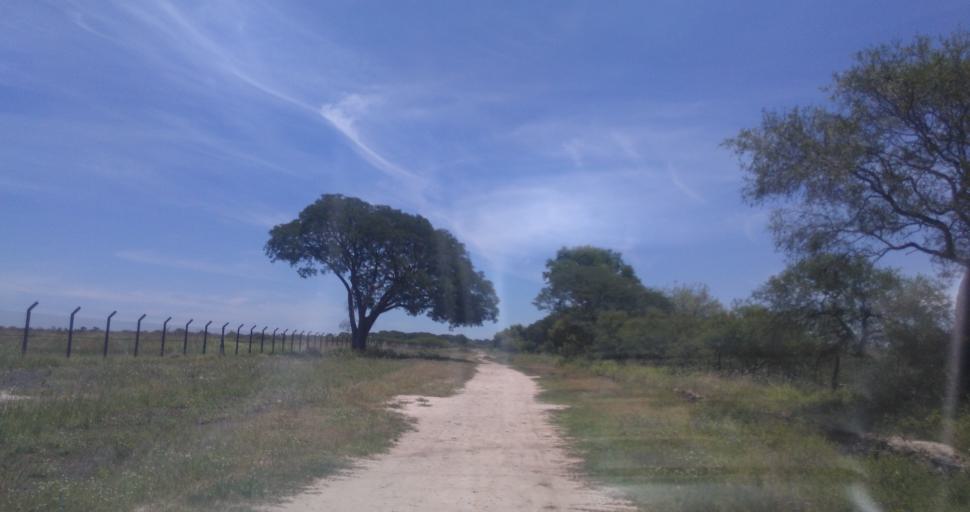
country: AR
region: Chaco
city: Fontana
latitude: -27.4304
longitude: -59.0460
